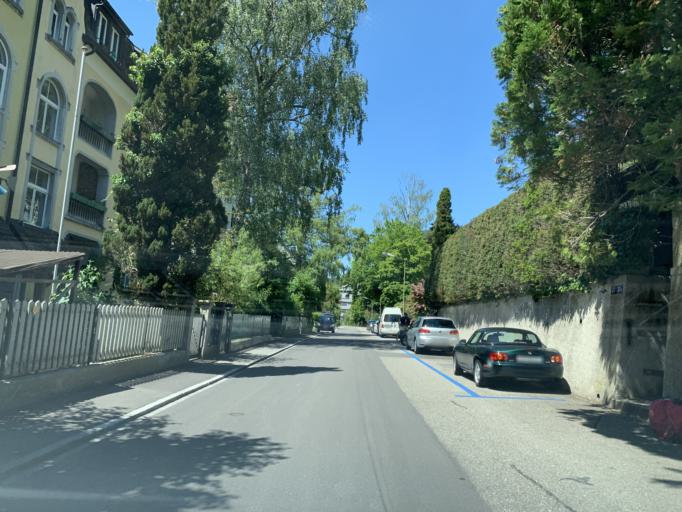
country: CH
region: Zurich
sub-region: Bezirk Winterthur
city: Stadt Winterthur (Kreis 1) / Lind
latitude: 47.5093
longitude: 8.7268
